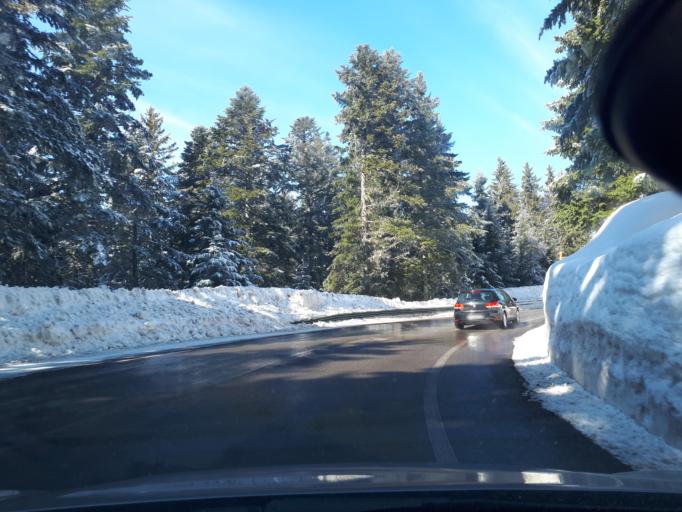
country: FR
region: Rhone-Alpes
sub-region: Departement de l'Isere
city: Vaulnaveys-le-Bas
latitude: 45.0986
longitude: 5.8676
